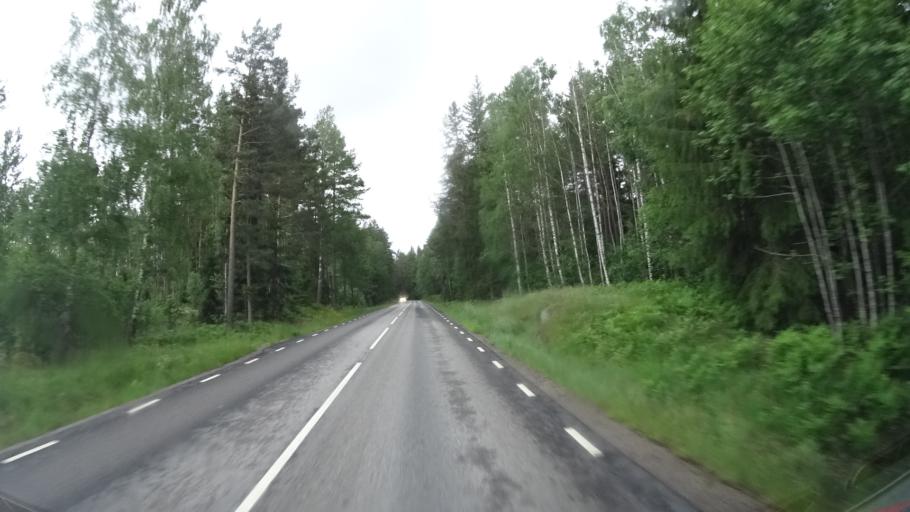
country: SE
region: Kalmar
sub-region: Oskarshamns Kommun
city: Oskarshamn
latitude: 57.3801
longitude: 16.2230
